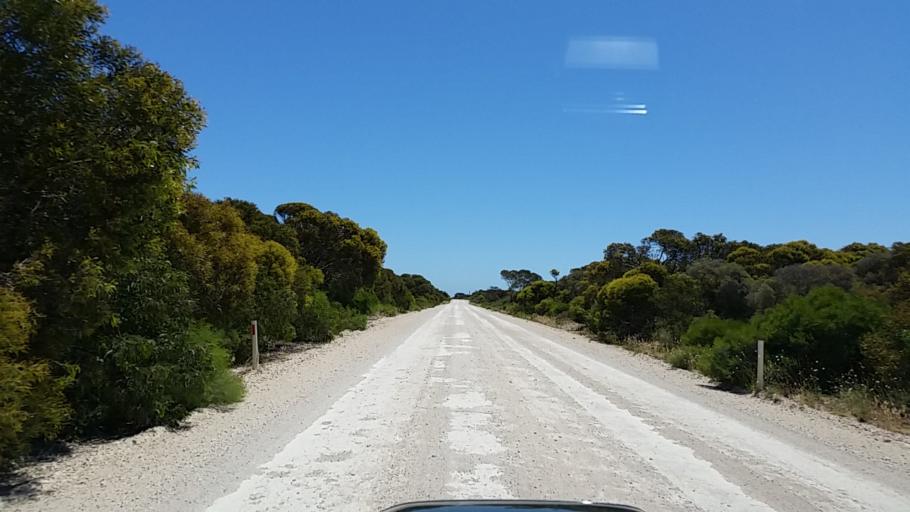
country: AU
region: South Australia
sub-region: Yorke Peninsula
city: Honiton
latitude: -35.2160
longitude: 137.0094
